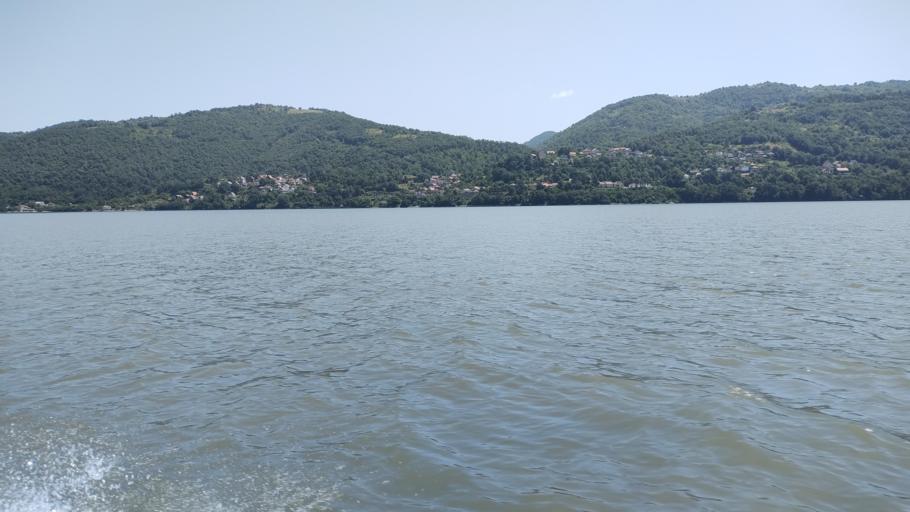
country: RO
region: Mehedinti
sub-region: Comuna Svinita
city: Svinita
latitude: 44.4990
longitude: 22.1894
